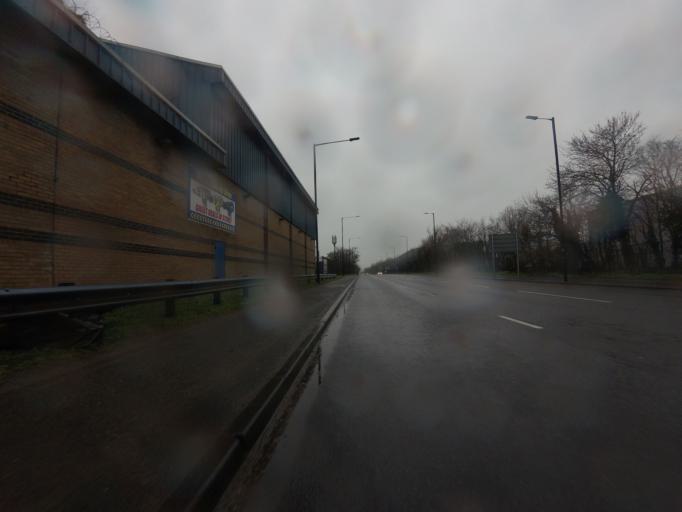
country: GB
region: England
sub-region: Hertfordshire
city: Waltham Cross
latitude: 51.6493
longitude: -0.0299
